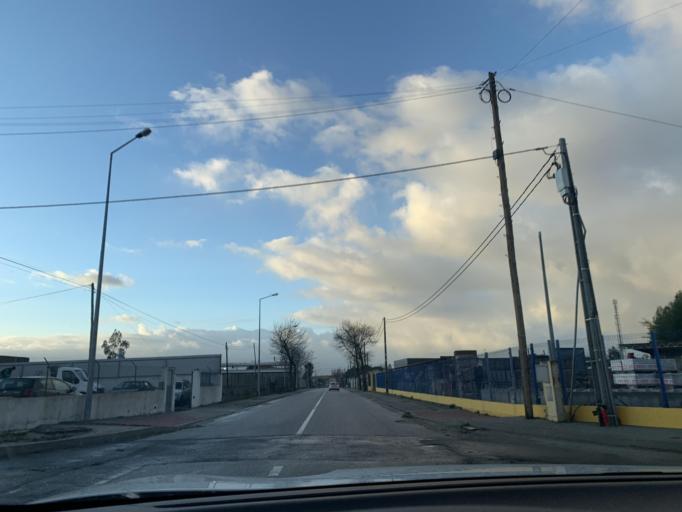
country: PT
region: Viseu
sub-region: Concelho de Tondela
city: Tondela
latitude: 40.4892
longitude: -8.0891
